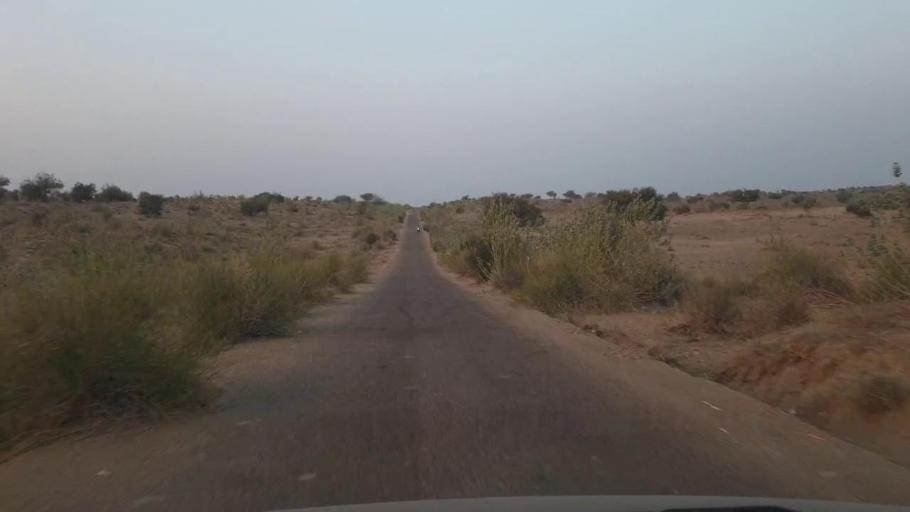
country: PK
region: Sindh
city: Umarkot
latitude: 25.3279
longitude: 70.0576
